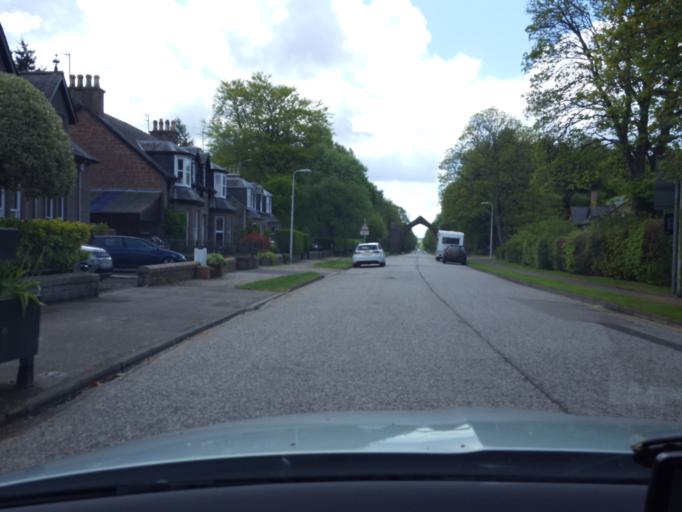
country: GB
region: Scotland
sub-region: Angus
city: Brechin
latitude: 56.8068
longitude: -2.6539
